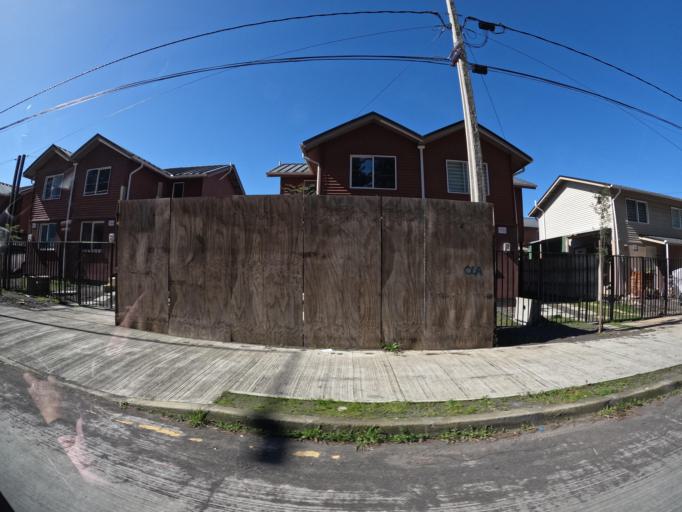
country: CL
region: Biobio
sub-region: Provincia de Concepcion
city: Concepcion
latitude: -36.8847
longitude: -73.1493
